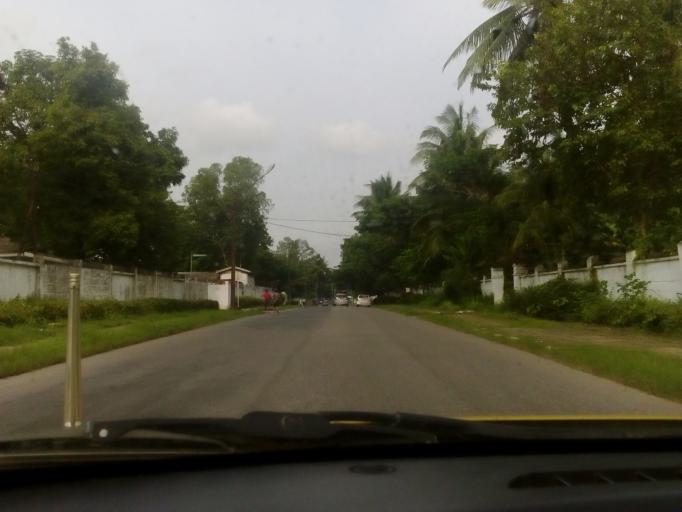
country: MM
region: Yangon
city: Yangon
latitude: 16.8428
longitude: 96.1540
